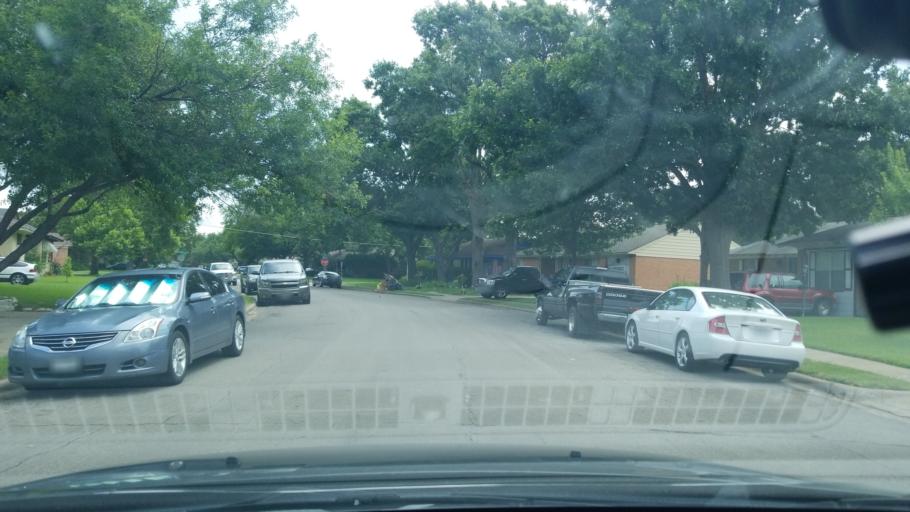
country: US
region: Texas
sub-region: Dallas County
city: Garland
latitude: 32.8309
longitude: -96.6794
